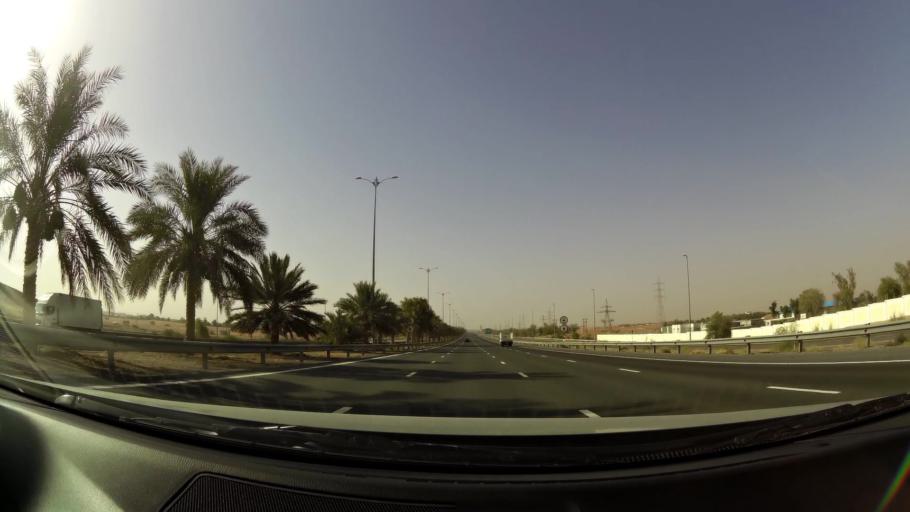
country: OM
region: Al Buraimi
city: Al Buraymi
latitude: 24.4837
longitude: 55.7734
